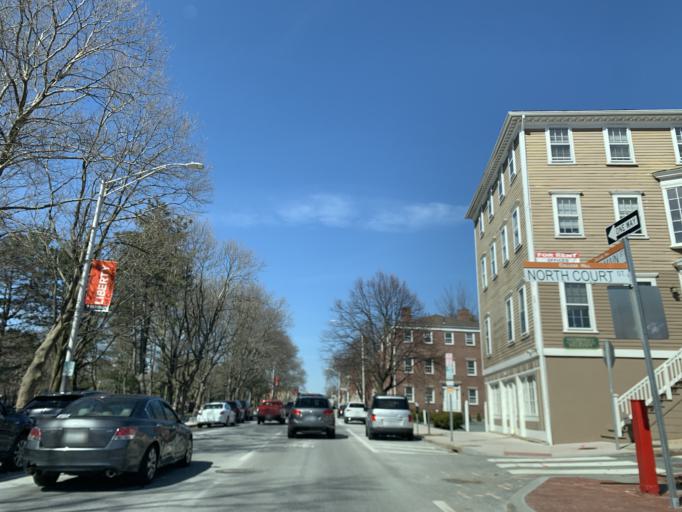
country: US
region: Rhode Island
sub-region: Providence County
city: Providence
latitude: 41.8290
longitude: -71.4097
